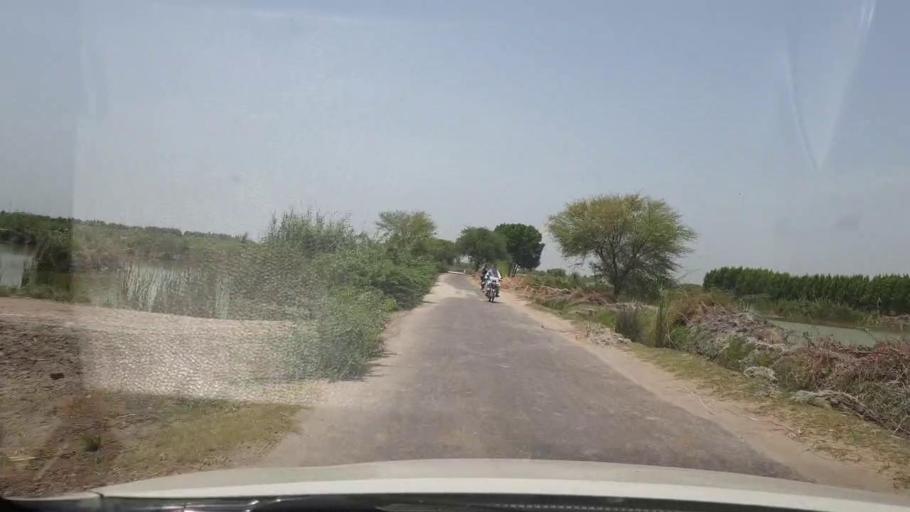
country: PK
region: Sindh
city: Bozdar
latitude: 27.2553
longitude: 68.6361
